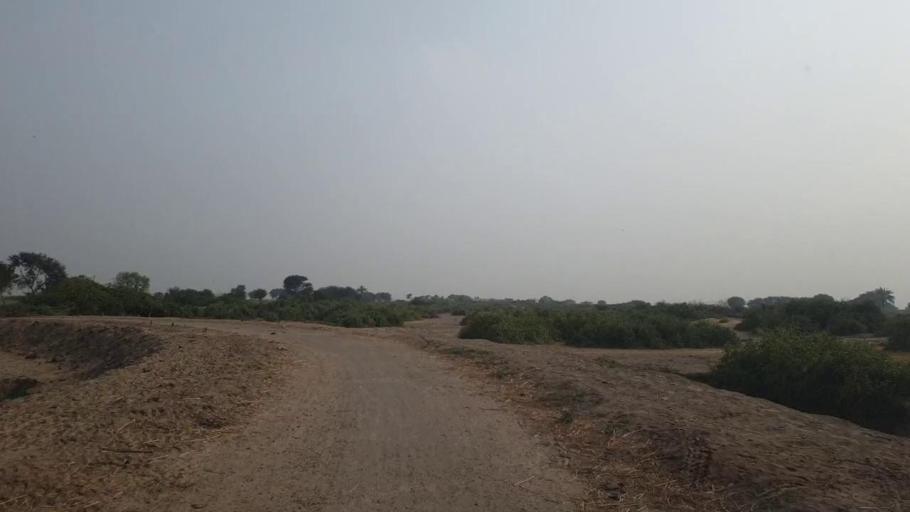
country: PK
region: Sindh
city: Mirpur Batoro
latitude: 24.6278
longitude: 68.4109
